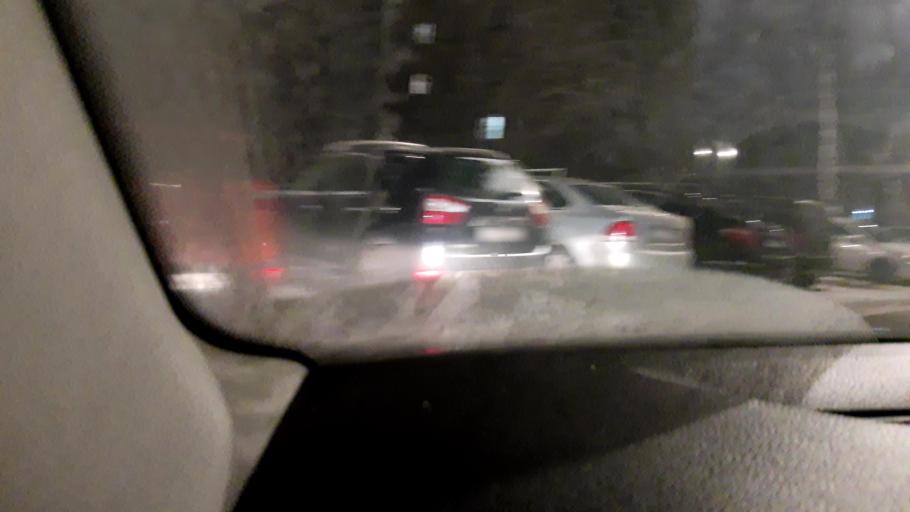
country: RU
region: Moskovskaya
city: Elektrostal'
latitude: 55.7644
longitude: 38.4443
